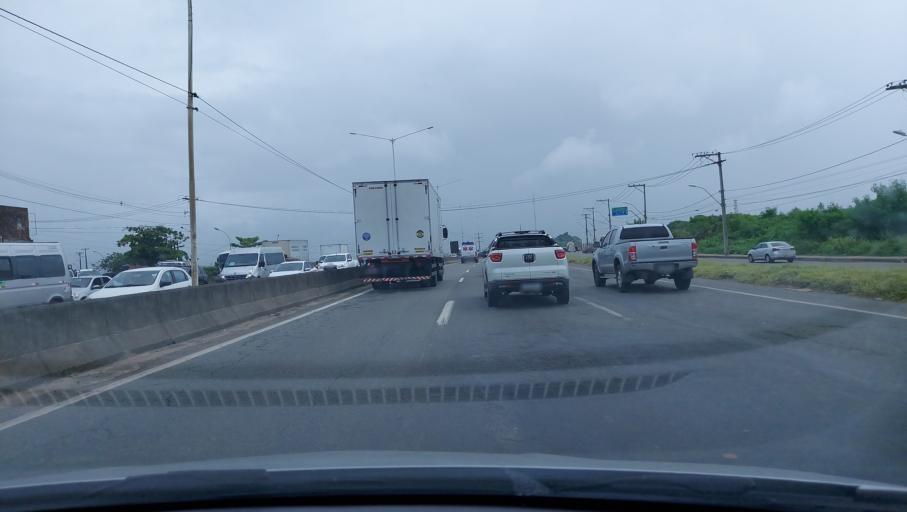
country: BR
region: Bahia
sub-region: Salvador
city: Salvador
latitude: -12.8914
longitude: -38.4456
